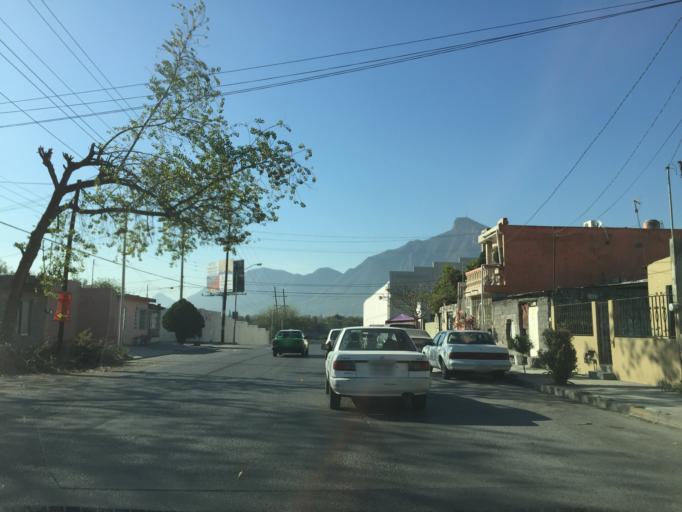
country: MX
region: Nuevo Leon
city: Guadalupe
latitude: 25.6931
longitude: -100.2173
